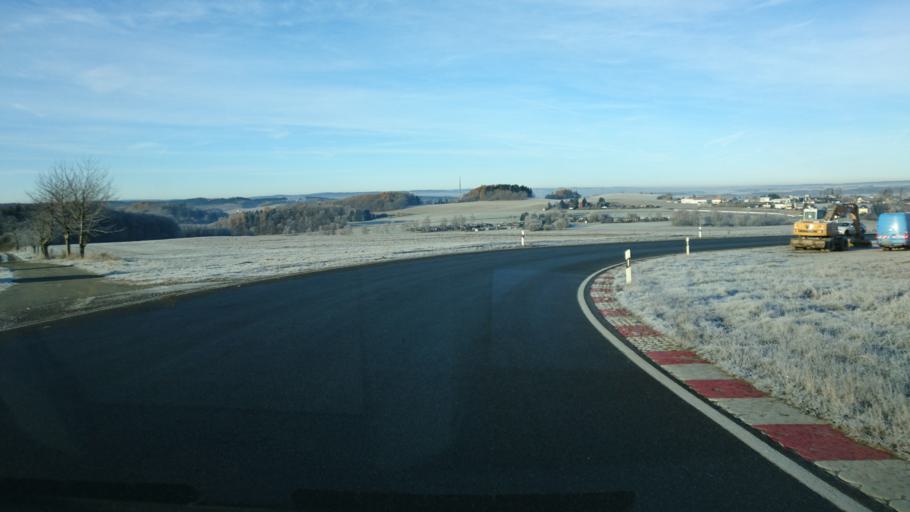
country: DE
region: Thuringia
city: Schleiz
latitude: 50.5646
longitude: 11.8210
